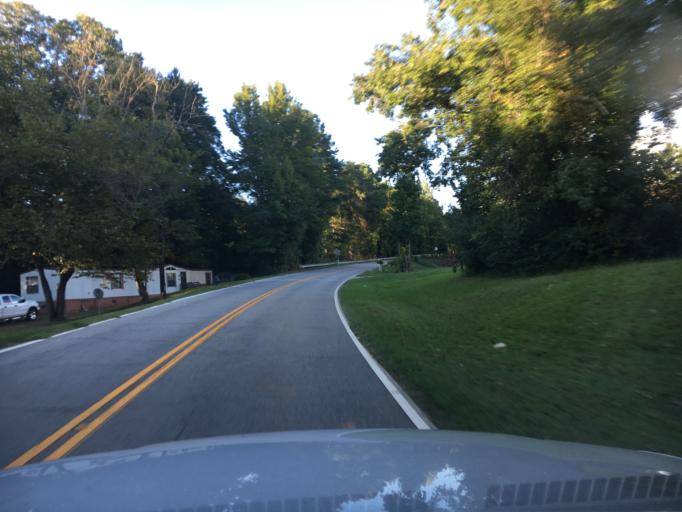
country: US
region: South Carolina
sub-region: Spartanburg County
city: Roebuck
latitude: 34.8962
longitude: -81.9941
